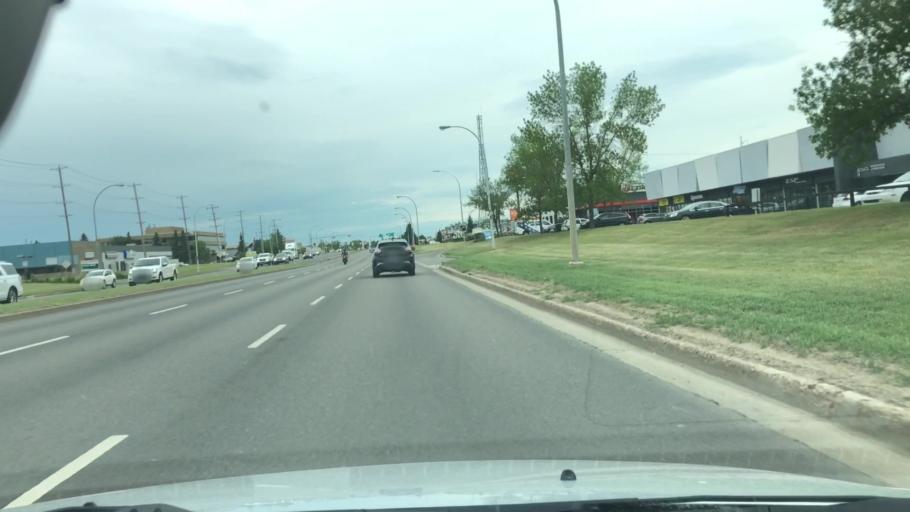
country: CA
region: Alberta
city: St. Albert
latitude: 53.5517
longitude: -113.6155
